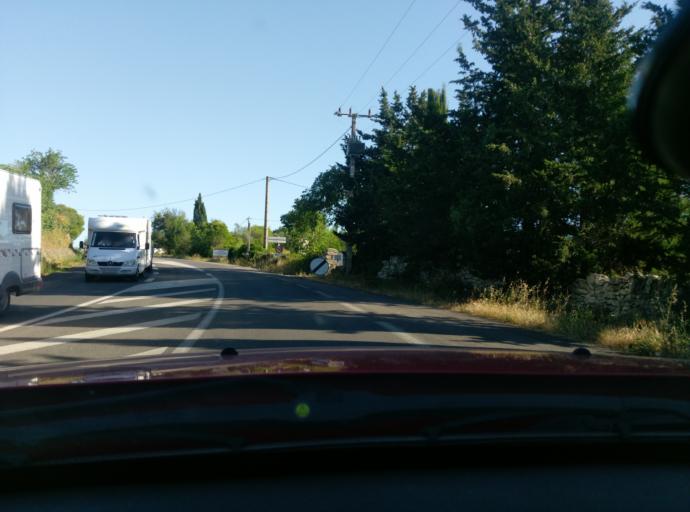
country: FR
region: Languedoc-Roussillon
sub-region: Departement du Gard
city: Uzes
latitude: 43.9942
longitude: 4.4190
